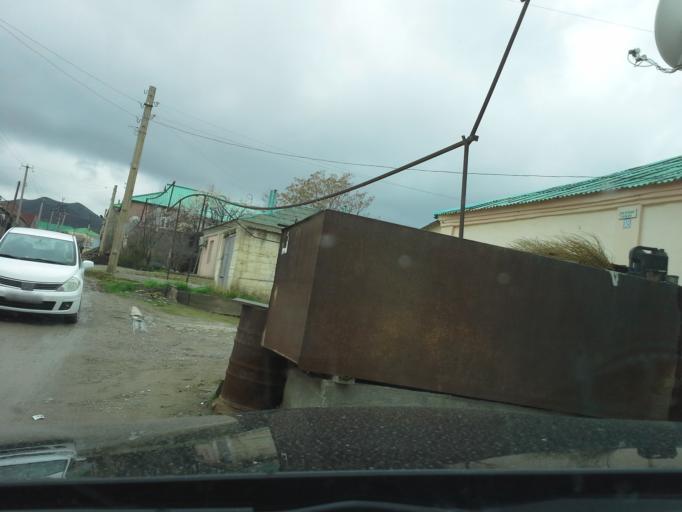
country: TM
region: Ahal
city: Abadan
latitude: 37.9579
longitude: 58.2113
